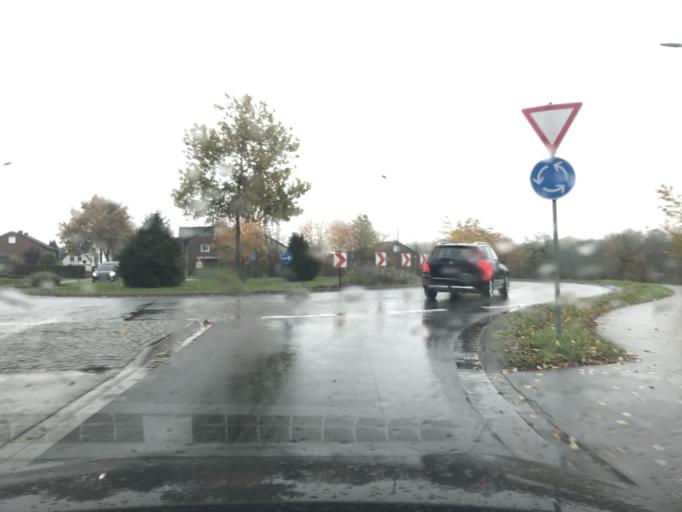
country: DE
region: North Rhine-Westphalia
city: Oelde
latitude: 51.8124
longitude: 8.1352
